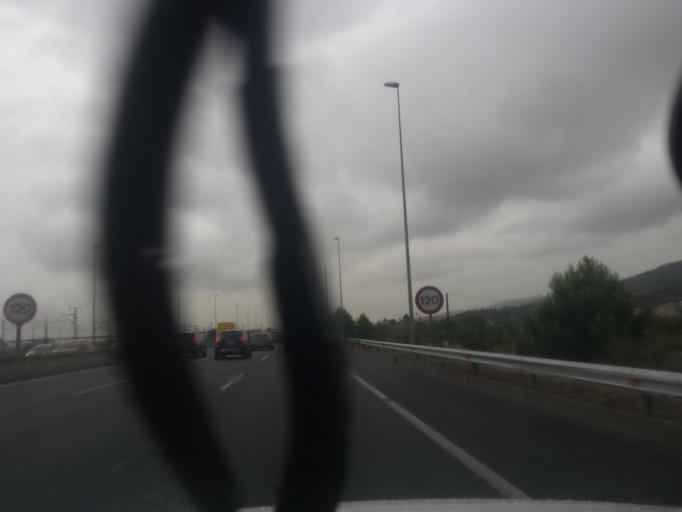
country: ES
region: Catalonia
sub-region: Provincia de Barcelona
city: Sant Vicenc dels Horts
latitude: 41.3972
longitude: 2.0156
